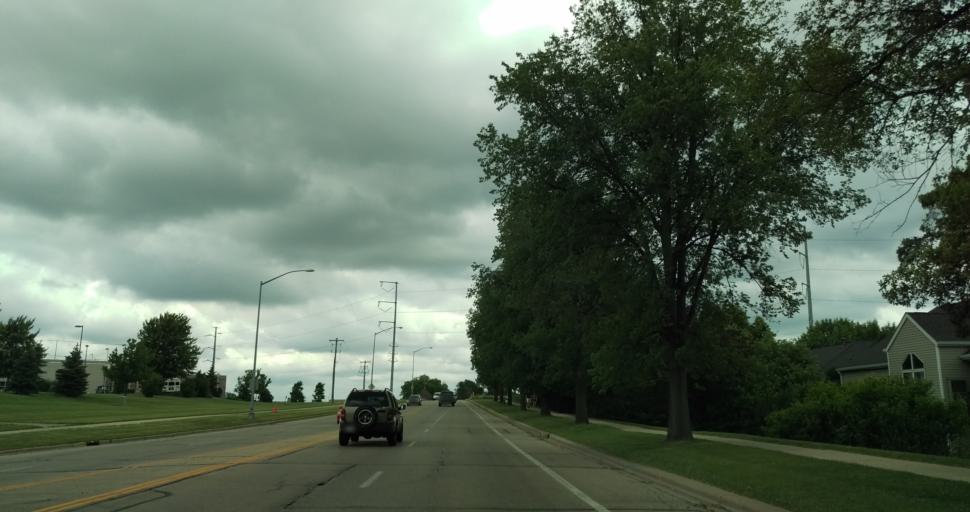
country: US
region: Wisconsin
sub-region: Dane County
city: Middleton
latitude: 43.0533
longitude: -89.5177
